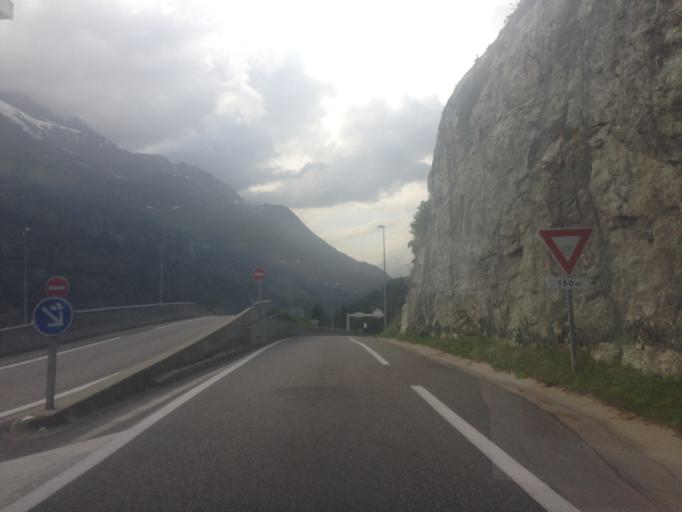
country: FR
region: Rhone-Alpes
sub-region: Departement de la Savoie
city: Tignes
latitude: 45.4976
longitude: 6.9328
